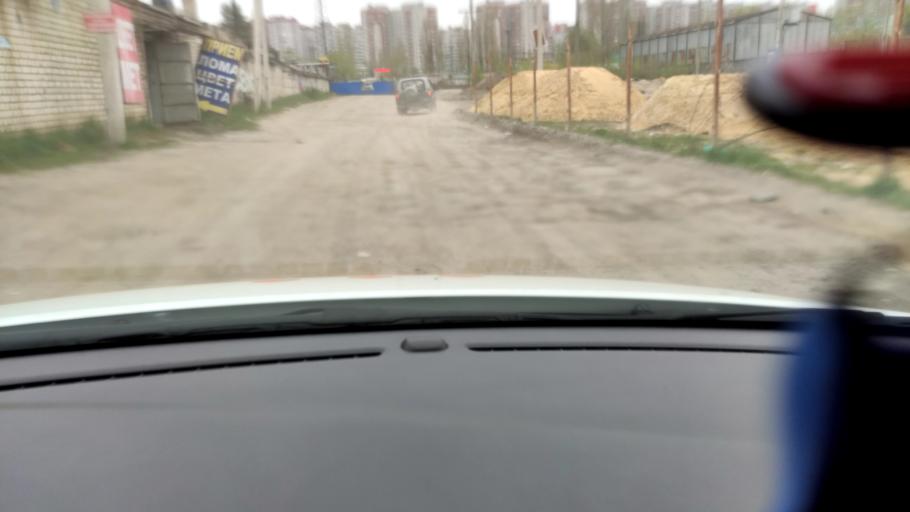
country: RU
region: Voronezj
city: Podgornoye
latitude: 51.7194
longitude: 39.1510
